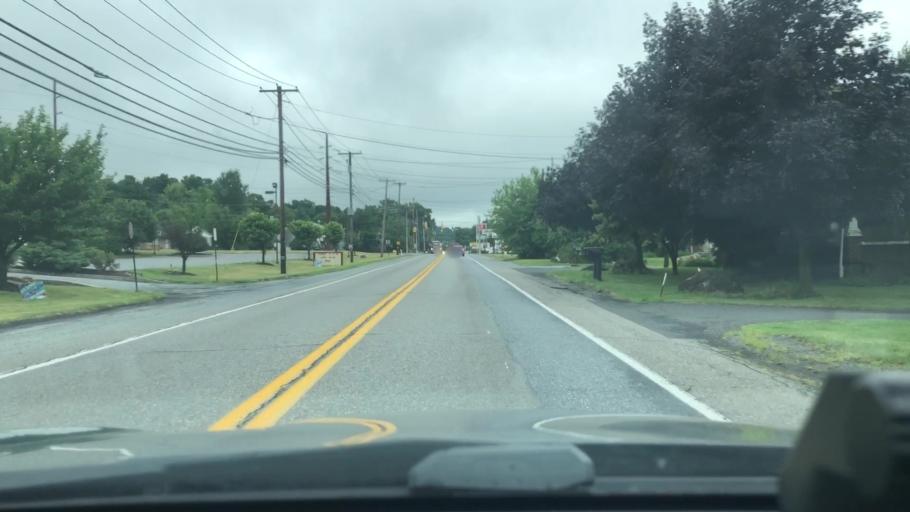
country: US
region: Pennsylvania
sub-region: Lehigh County
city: Emmaus
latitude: 40.5225
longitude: -75.5189
